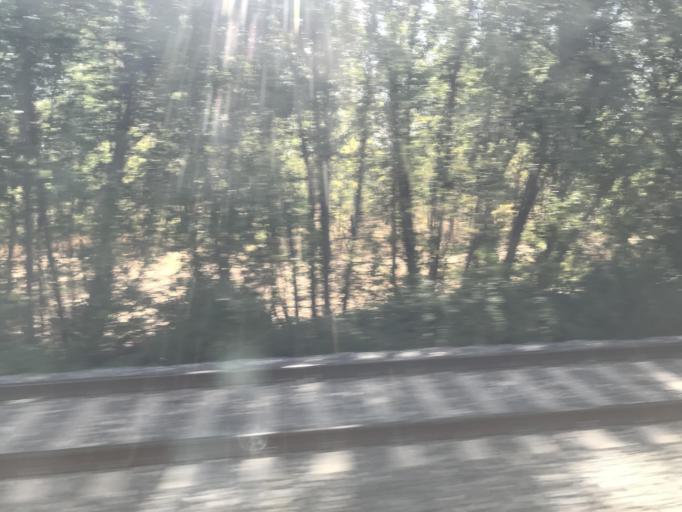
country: ES
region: Castille and Leon
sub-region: Provincia de Palencia
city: Soto de Cerrato
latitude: 41.9796
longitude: -4.4296
